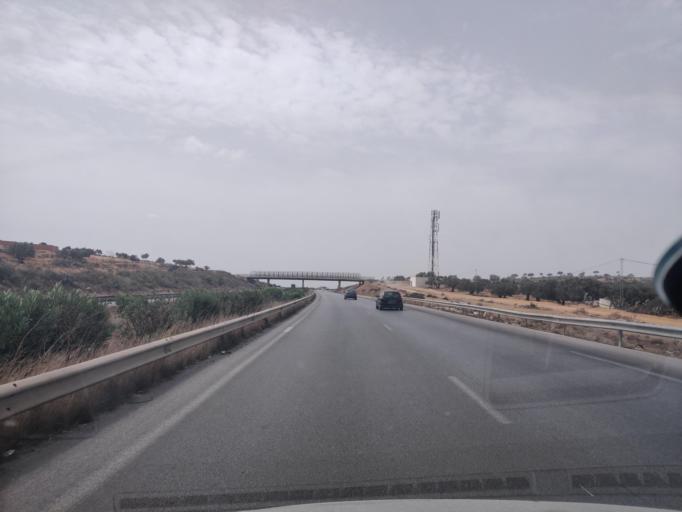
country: TN
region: Susah
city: Sidi Bou Ali
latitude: 35.9603
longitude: 10.4929
